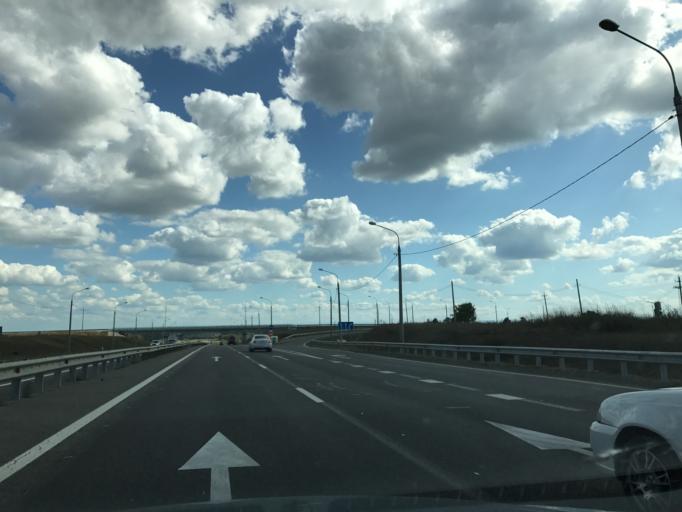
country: RU
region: Adygeya
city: Adygeysk
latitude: 44.8464
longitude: 39.2066
